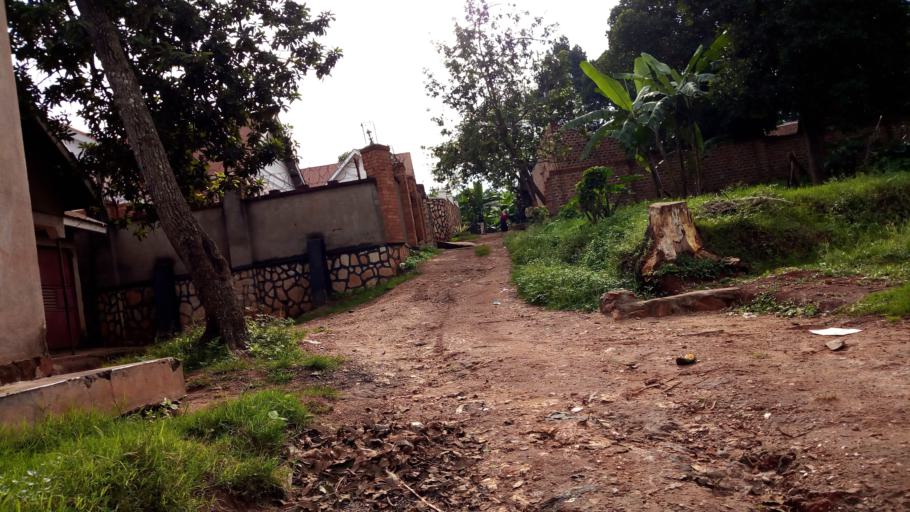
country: UG
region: Central Region
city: Kampala Central Division
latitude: 0.3719
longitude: 32.5548
